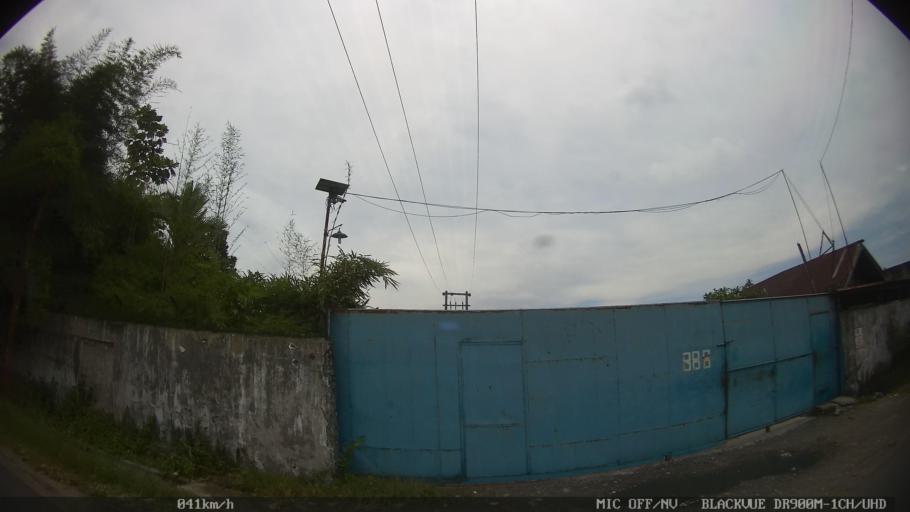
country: ID
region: North Sumatra
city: Binjai
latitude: 3.6101
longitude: 98.5541
